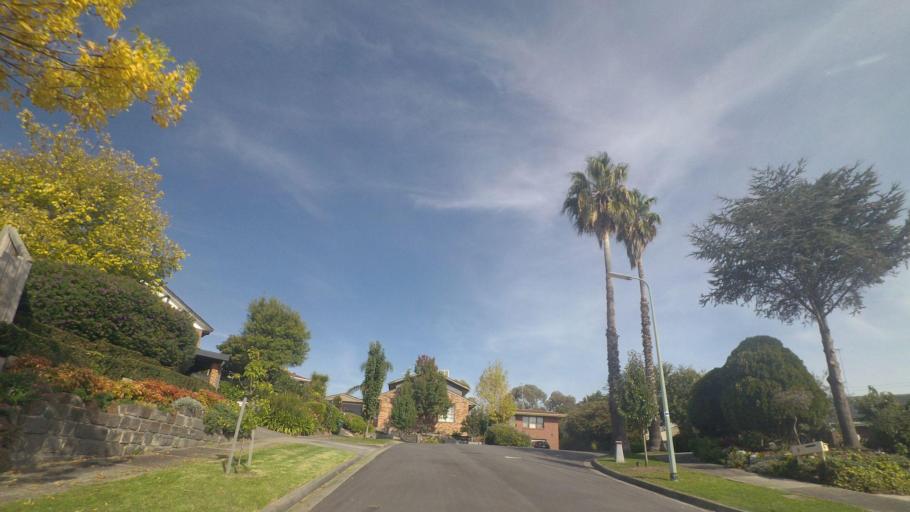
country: AU
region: Victoria
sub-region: Manningham
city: Doncaster East
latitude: -37.7722
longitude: 145.1462
